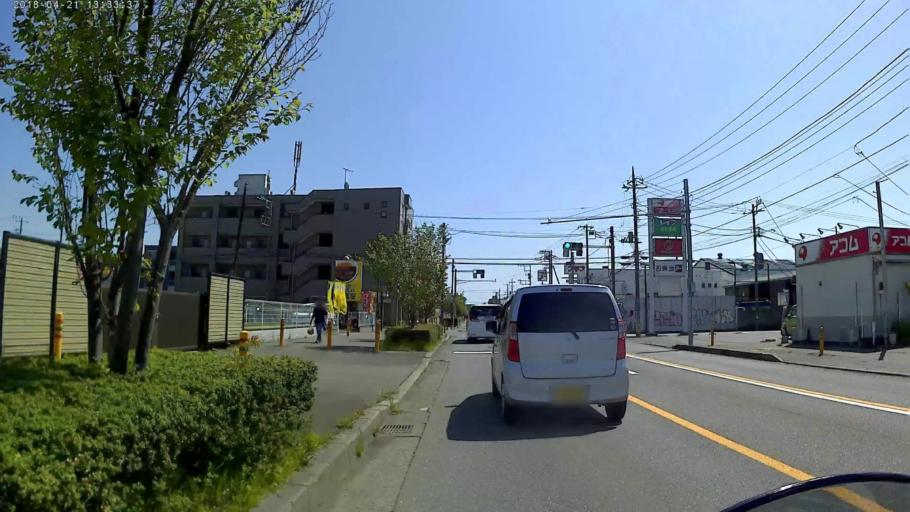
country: JP
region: Kanagawa
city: Atsugi
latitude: 35.3971
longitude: 139.3810
